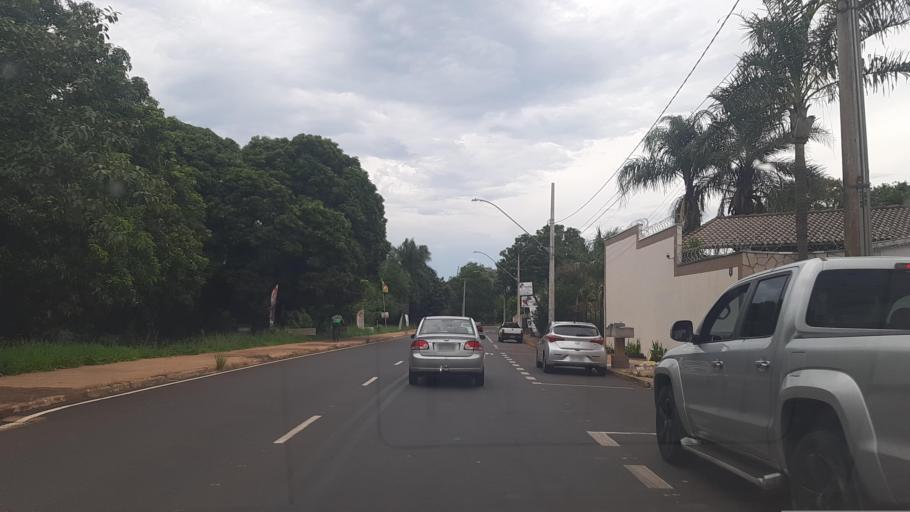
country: BR
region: Minas Gerais
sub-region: Uberlandia
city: Uberlandia
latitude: -18.9280
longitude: -48.2942
